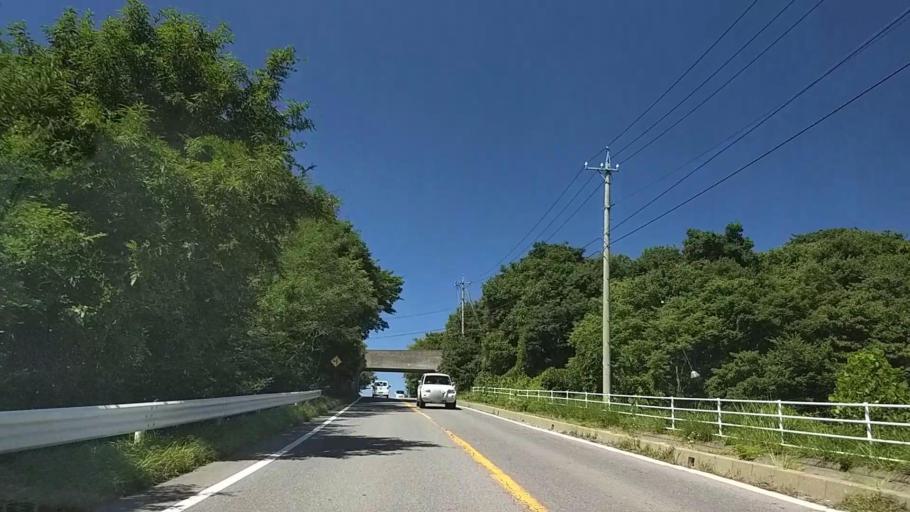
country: JP
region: Nagano
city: Komoro
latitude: 36.3492
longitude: 138.4226
